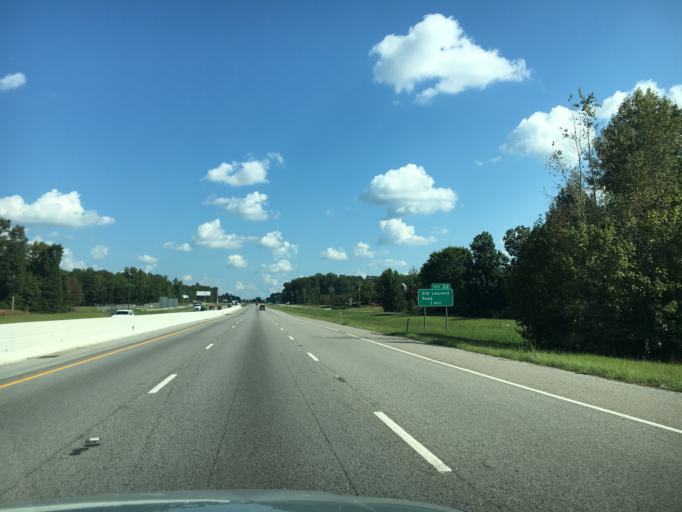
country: US
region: South Carolina
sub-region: Greenville County
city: Fountain Inn
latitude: 34.6780
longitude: -82.1997
